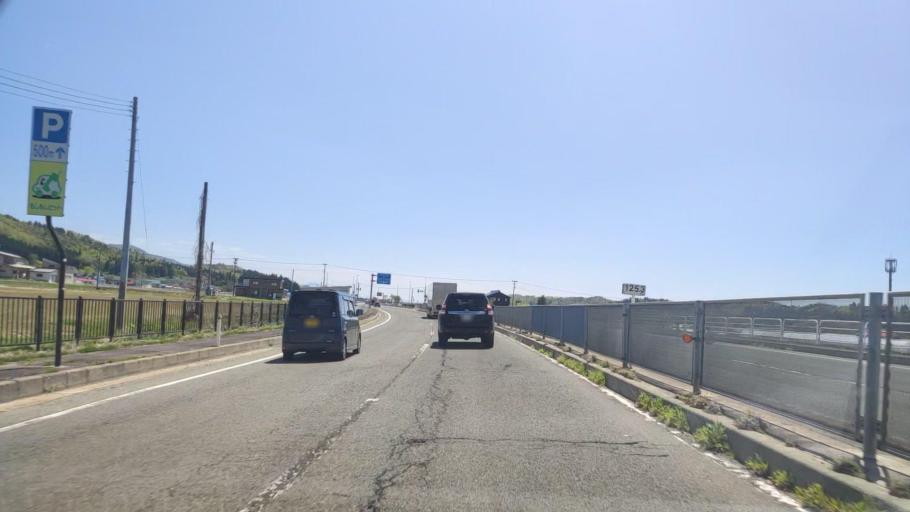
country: JP
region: Yamagata
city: Obanazawa
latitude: 38.5514
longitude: 140.3967
